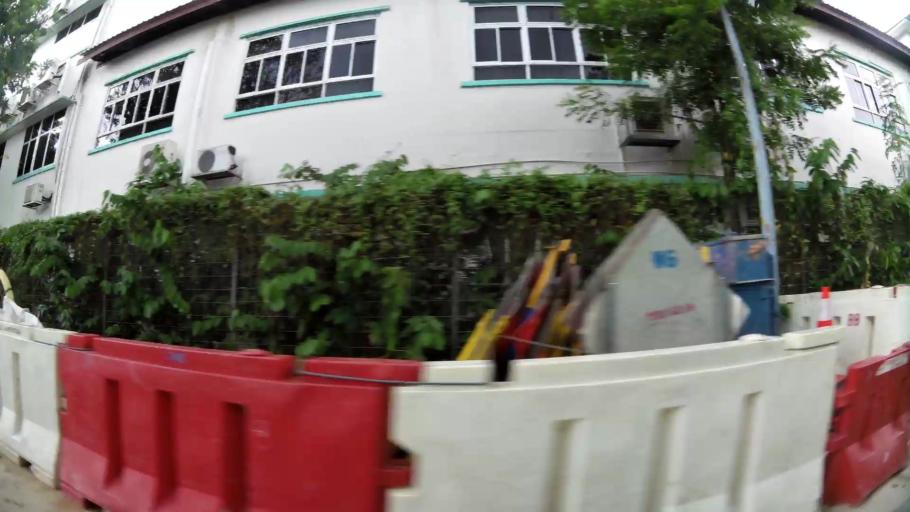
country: SG
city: Singapore
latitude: 1.3123
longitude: 103.8481
